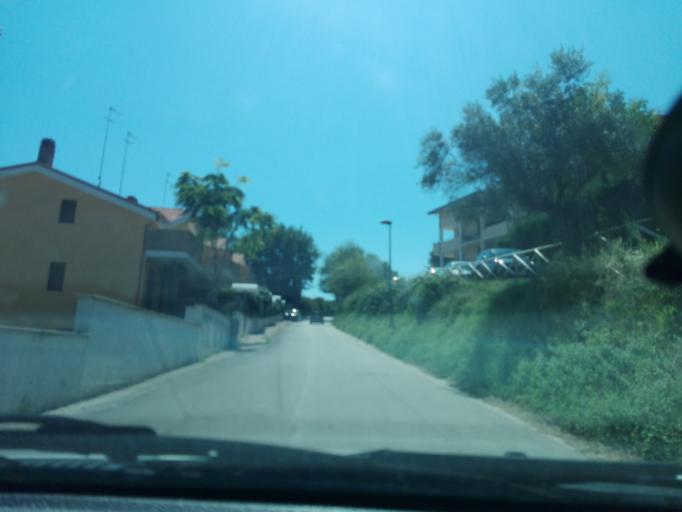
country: IT
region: Abruzzo
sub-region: Provincia di Pescara
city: Montesilvano Marina
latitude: 42.4947
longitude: 14.1607
